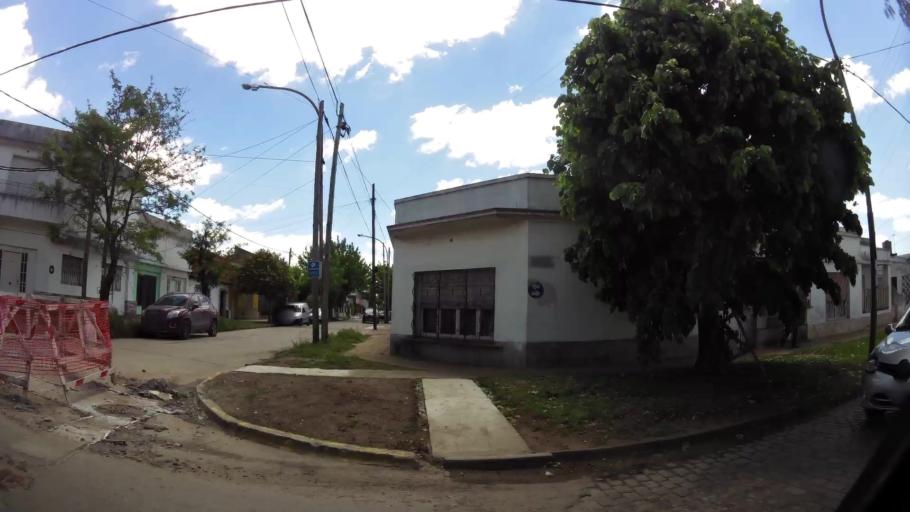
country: AR
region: Buenos Aires
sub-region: Partido de Lomas de Zamora
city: Lomas de Zamora
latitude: -34.7314
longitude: -58.4112
